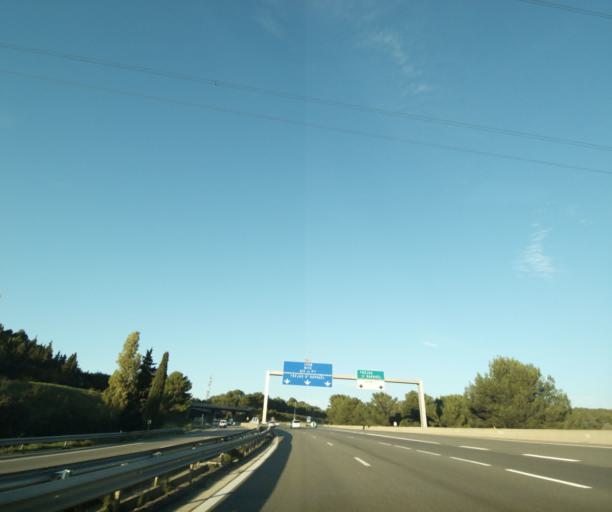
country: FR
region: Provence-Alpes-Cote d'Azur
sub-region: Departement des Bouches-du-Rhone
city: Roquevaire
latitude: 43.3510
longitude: 5.6203
